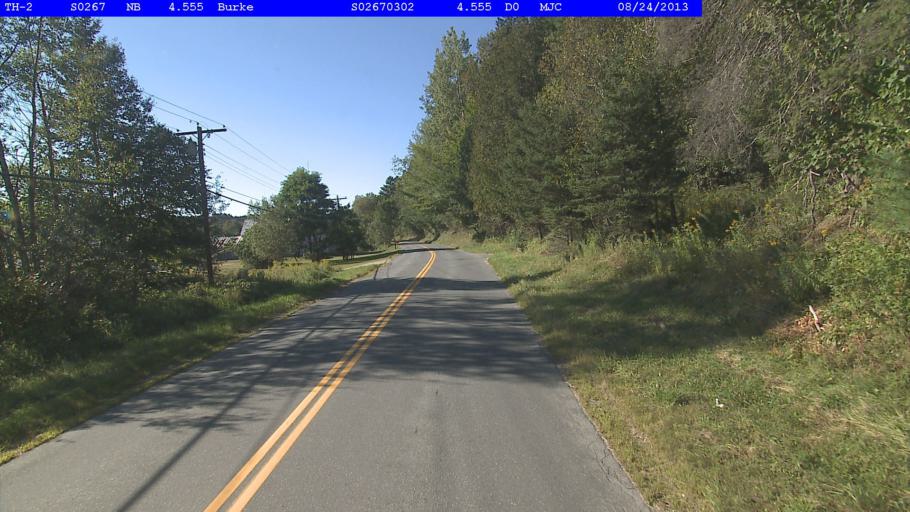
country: US
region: Vermont
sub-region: Caledonia County
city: Lyndonville
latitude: 44.6386
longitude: -71.9739
